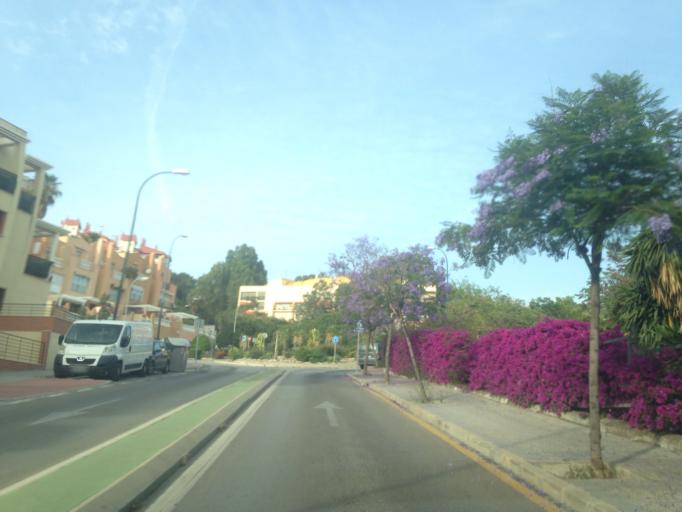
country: ES
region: Andalusia
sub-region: Provincia de Malaga
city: Malaga
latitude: 36.7365
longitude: -4.4152
